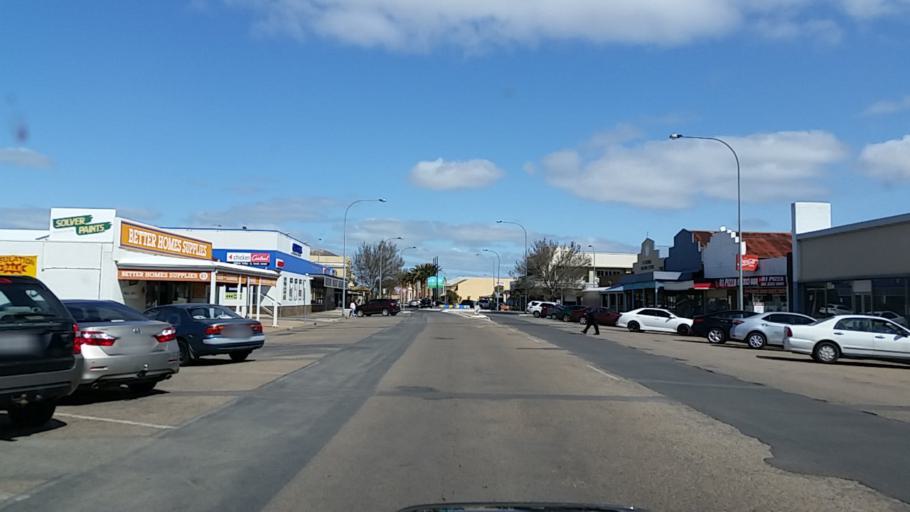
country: AU
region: South Australia
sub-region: Port Pirie City and Dists
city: Port Pirie
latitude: -33.1764
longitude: 138.0085
